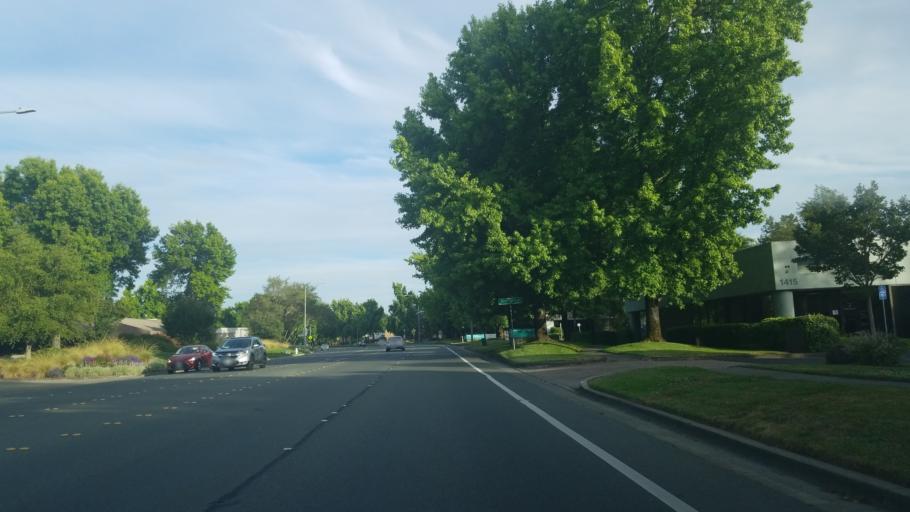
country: US
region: California
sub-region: Sonoma County
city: Santa Rosa
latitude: 38.4518
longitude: -122.7352
